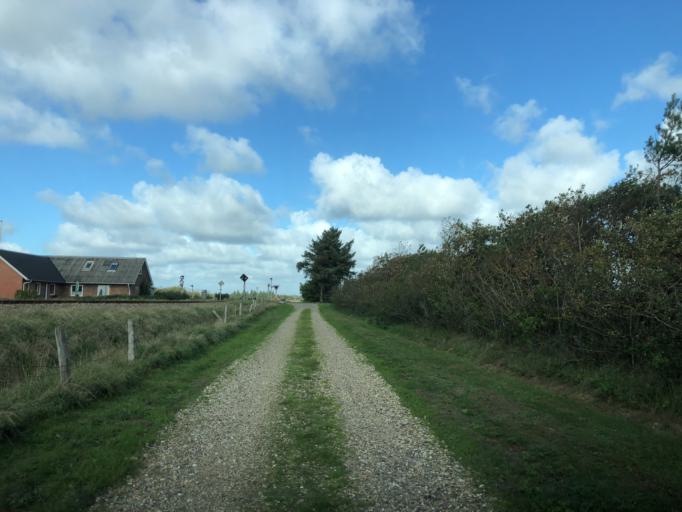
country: DK
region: Central Jutland
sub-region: Holstebro Kommune
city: Ulfborg
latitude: 56.2880
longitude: 8.3295
